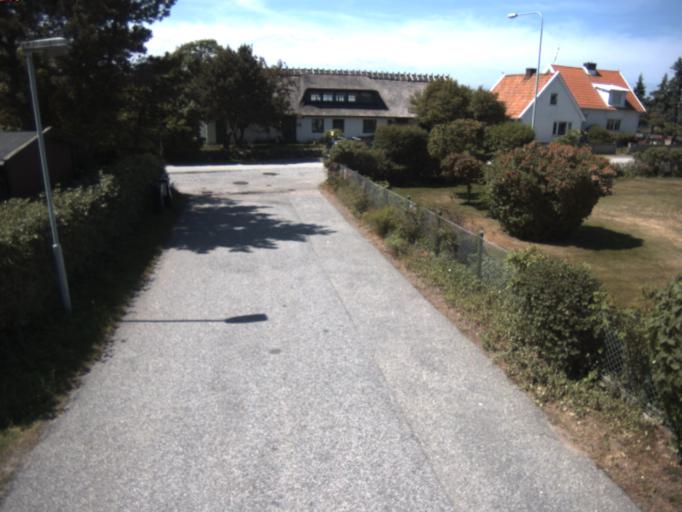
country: DK
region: Capital Region
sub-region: Helsingor Kommune
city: Hellebaek
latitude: 56.1204
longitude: 12.6051
